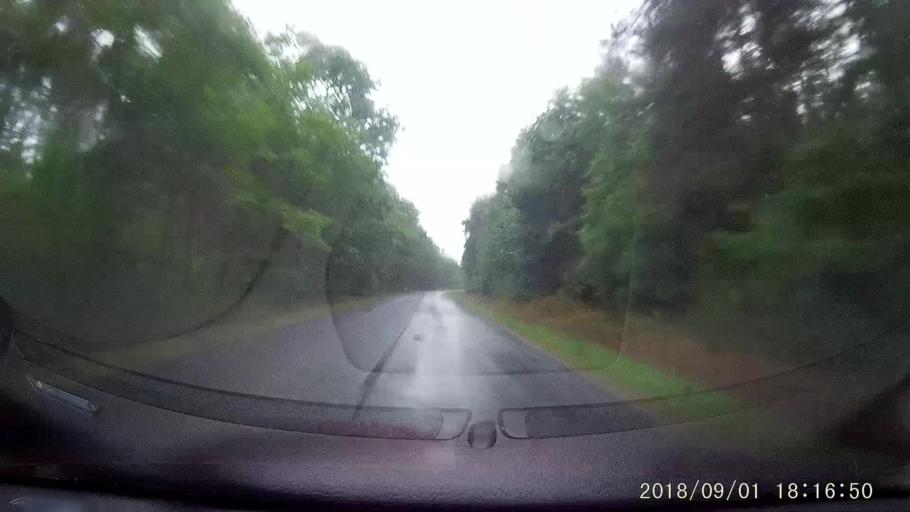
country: PL
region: Lower Silesian Voivodeship
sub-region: Powiat zgorzelecki
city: Piensk
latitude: 51.2686
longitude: 15.0525
